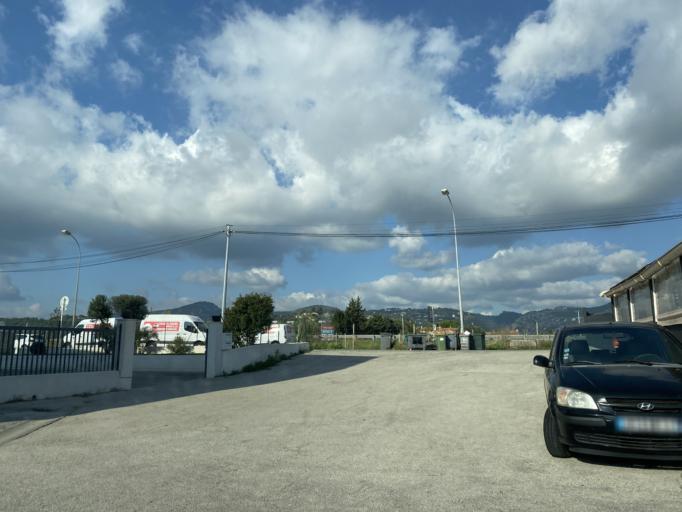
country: FR
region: Provence-Alpes-Cote d'Azur
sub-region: Departement du Var
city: Ollioules
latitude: 43.1198
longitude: 5.8453
